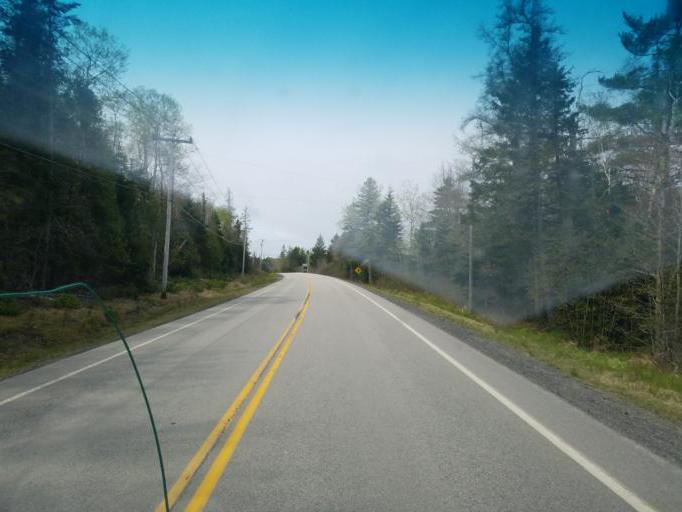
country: US
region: Maine
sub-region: Washington County
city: Eastport
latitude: 44.7997
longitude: -67.1423
